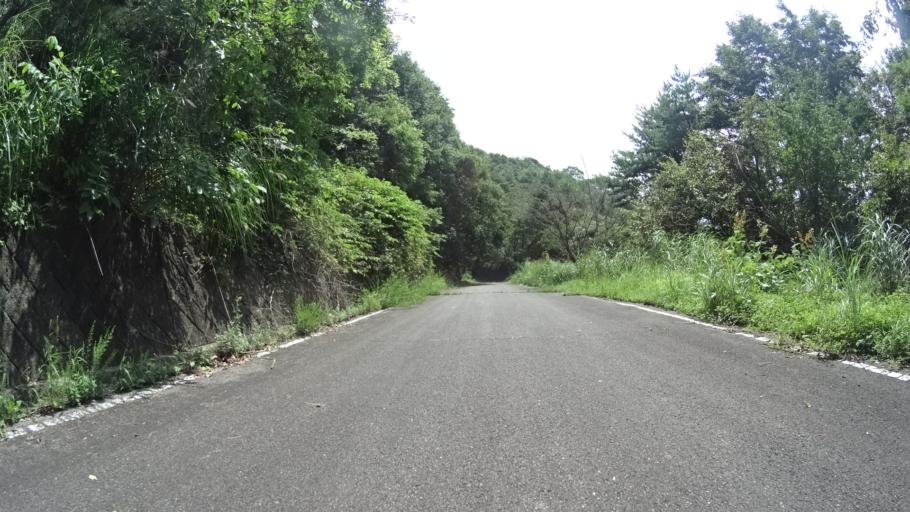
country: JP
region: Yamanashi
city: Nirasaki
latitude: 35.8823
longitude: 138.4945
